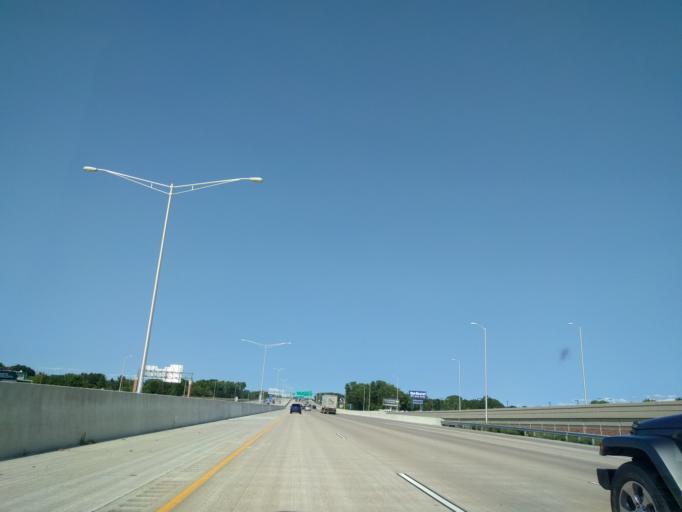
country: US
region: Wisconsin
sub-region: Brown County
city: Howard
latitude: 44.5418
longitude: -88.0741
